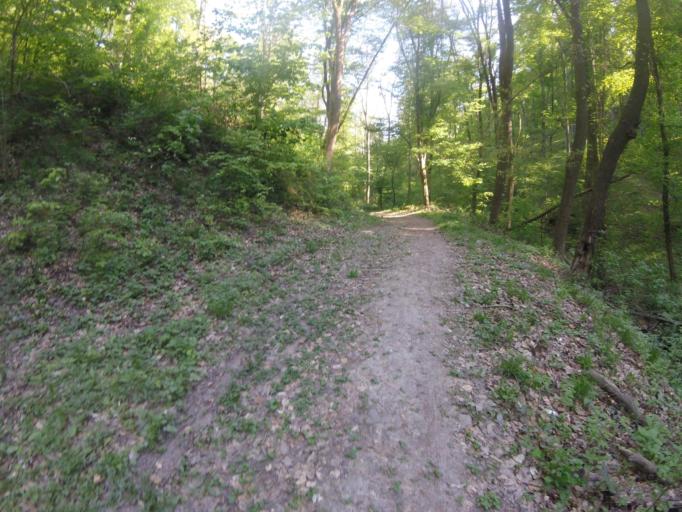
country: HU
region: Pest
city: Pilisszentkereszt
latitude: 47.7094
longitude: 18.8945
